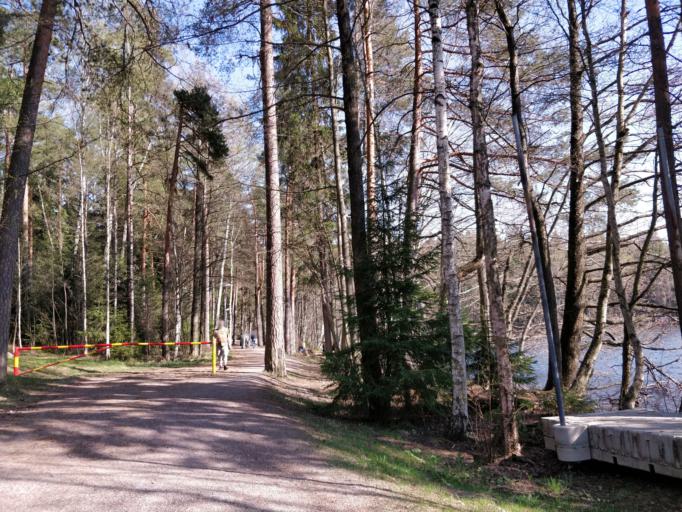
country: FI
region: Uusimaa
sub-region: Helsinki
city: Vantaa
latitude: 60.3135
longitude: 25.1153
